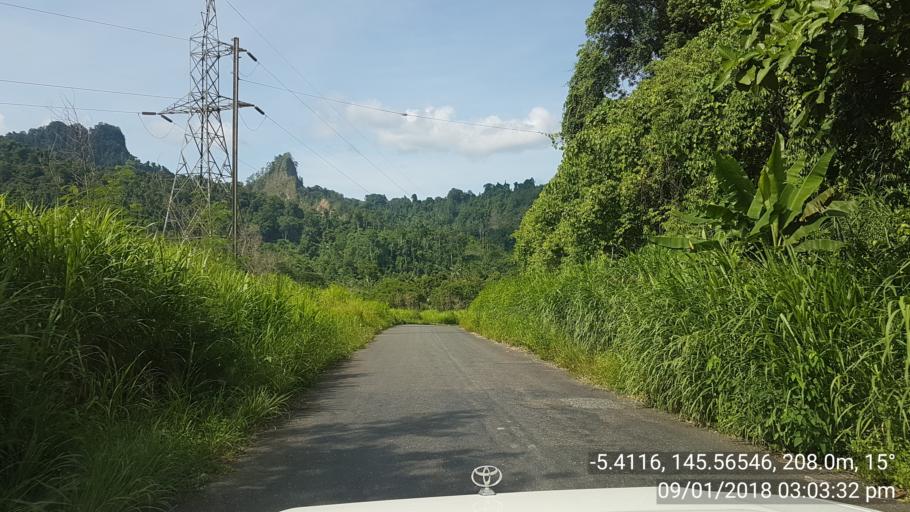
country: PG
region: Madang
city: Madang
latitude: -5.4117
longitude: 145.5656
